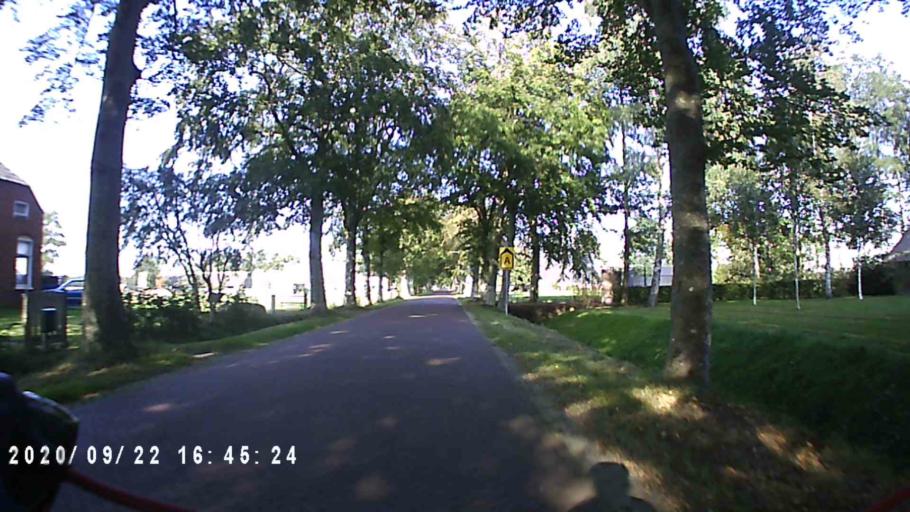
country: NL
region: Groningen
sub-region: Gemeente Leek
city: Leek
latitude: 53.1260
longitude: 6.4672
